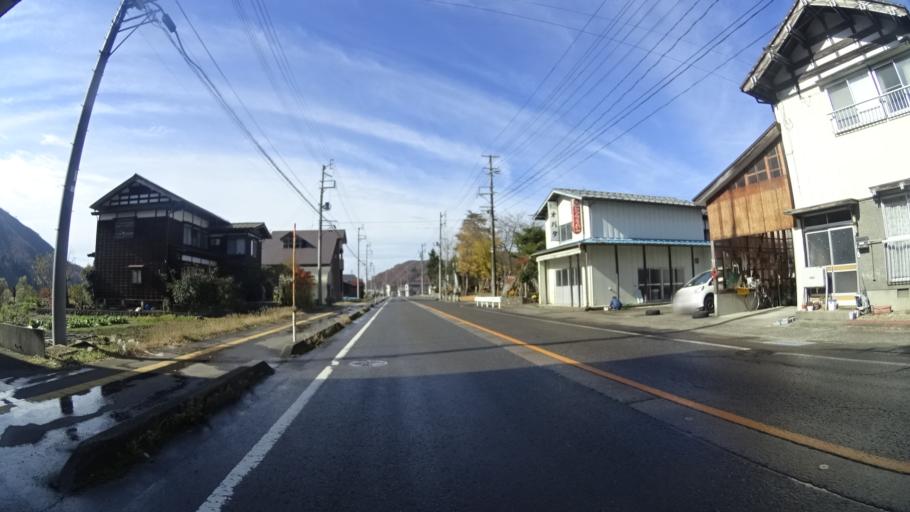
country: JP
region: Niigata
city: Muikamachi
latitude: 37.2259
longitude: 139.0078
